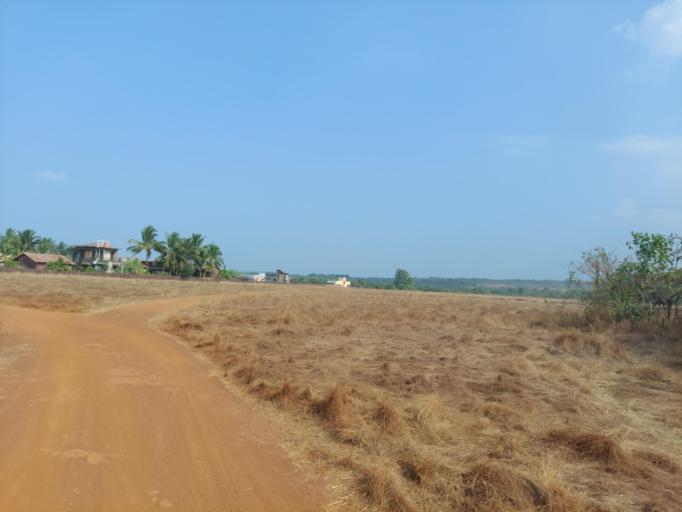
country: IN
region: Maharashtra
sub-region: Ratnagiri
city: Ratnagiri
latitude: 16.9256
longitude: 73.3187
